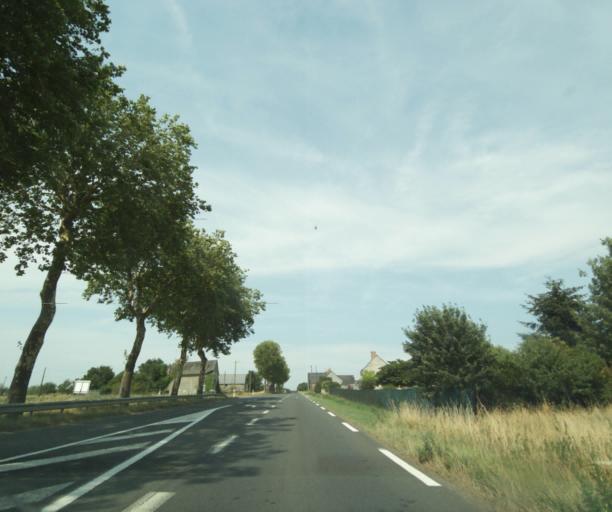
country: FR
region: Centre
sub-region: Departement d'Indre-et-Loire
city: Sainte-Maure-de-Touraine
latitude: 47.1306
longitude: 0.6324
